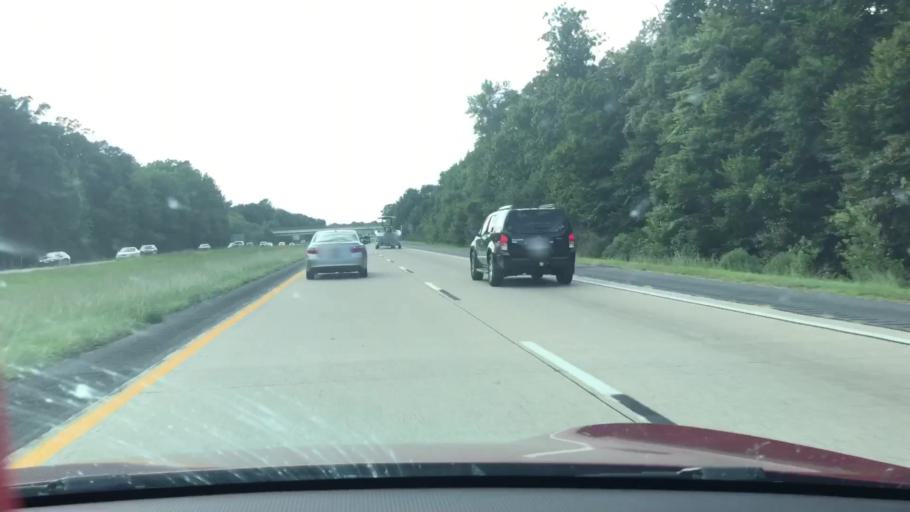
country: US
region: Delaware
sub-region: Kent County
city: Cheswold
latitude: 39.2193
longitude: -75.5608
